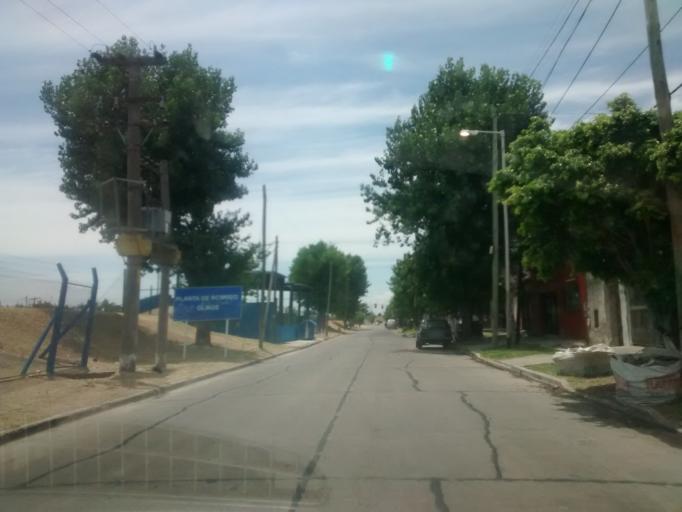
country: AR
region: Buenos Aires
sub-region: Partido de Avellaneda
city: Avellaneda
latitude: -34.6881
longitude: -58.3235
